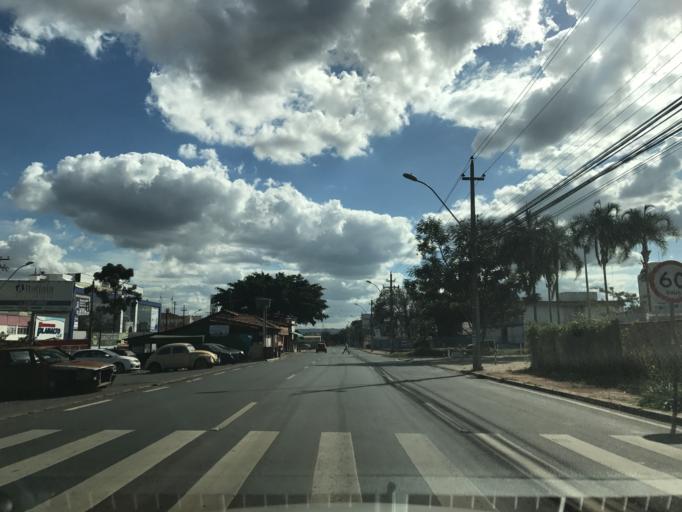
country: BR
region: Federal District
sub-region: Brasilia
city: Brasilia
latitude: -15.8031
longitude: -47.9646
